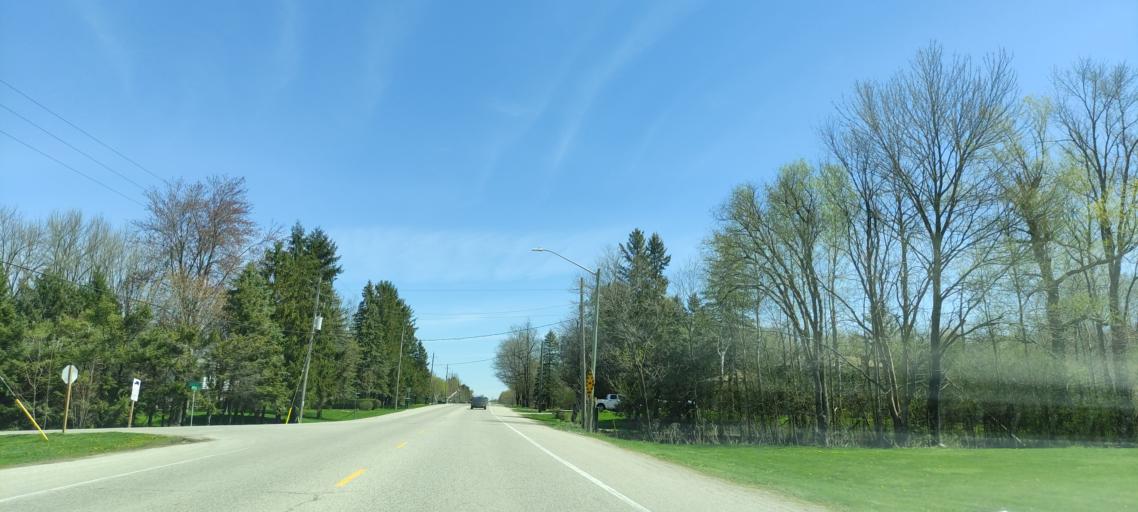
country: CA
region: Ontario
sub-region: Wellington County
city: Guelph
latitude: 43.5961
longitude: -80.3414
